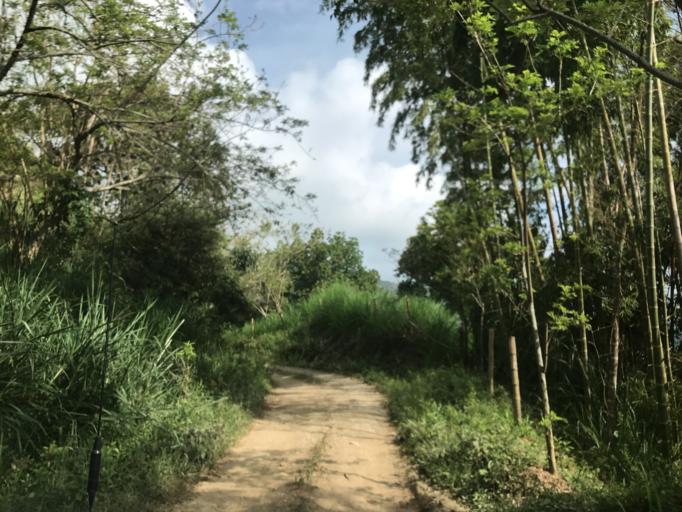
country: CO
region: Valle del Cauca
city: Obando
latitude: 4.5733
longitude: -75.8787
